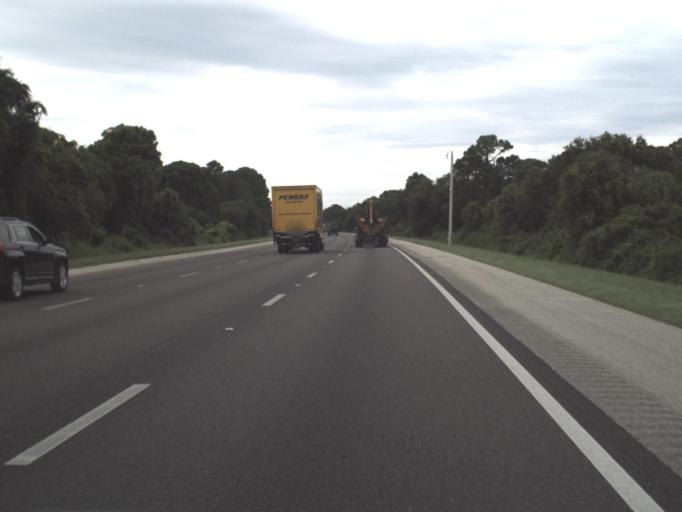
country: US
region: Florida
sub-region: Sarasota County
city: Vamo
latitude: 27.2364
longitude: -82.4527
